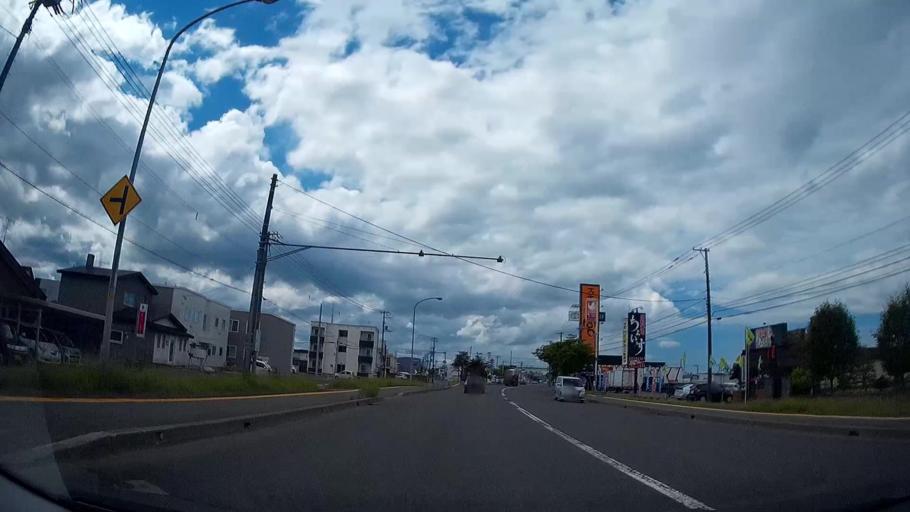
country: JP
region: Hokkaido
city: Chitose
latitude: 42.8718
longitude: 141.5863
